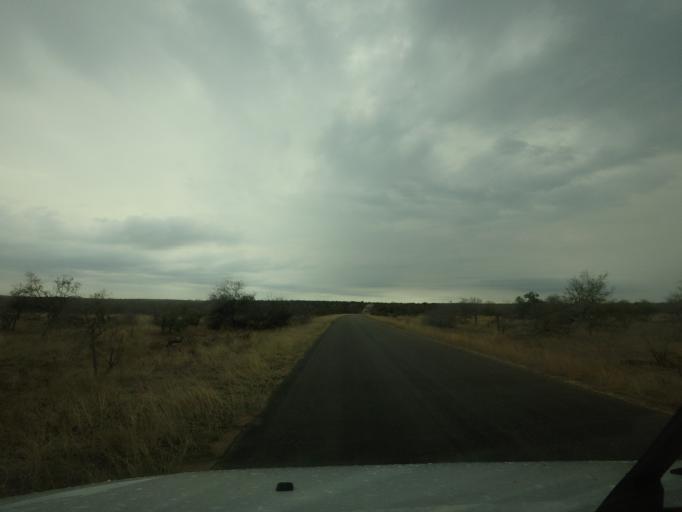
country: ZA
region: Limpopo
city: Thulamahashi
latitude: -24.4686
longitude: 31.4402
